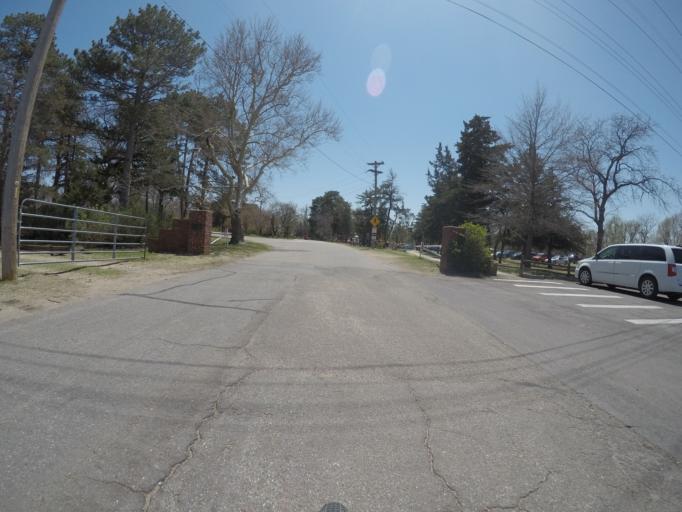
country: US
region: Kansas
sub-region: Pratt County
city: Pratt
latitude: 37.6362
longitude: -98.7357
